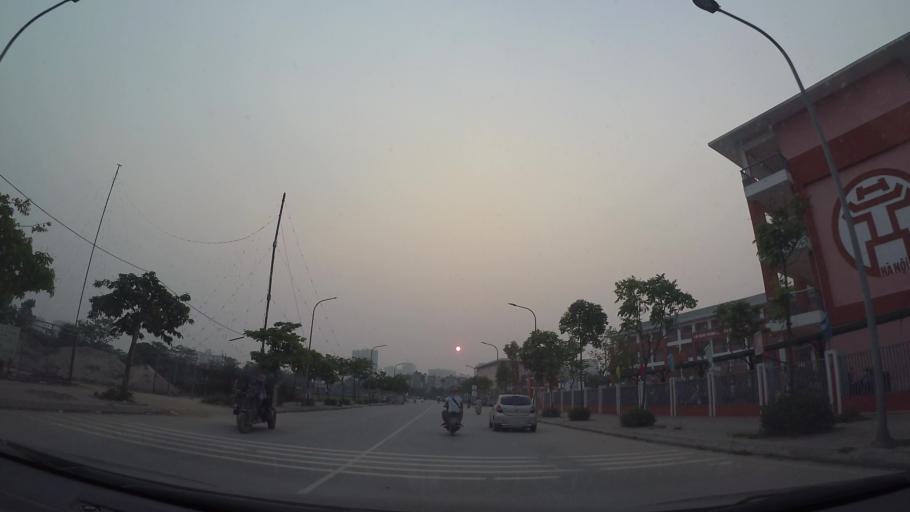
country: VN
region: Ha Noi
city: Thanh Xuan
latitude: 20.9772
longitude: 105.8020
